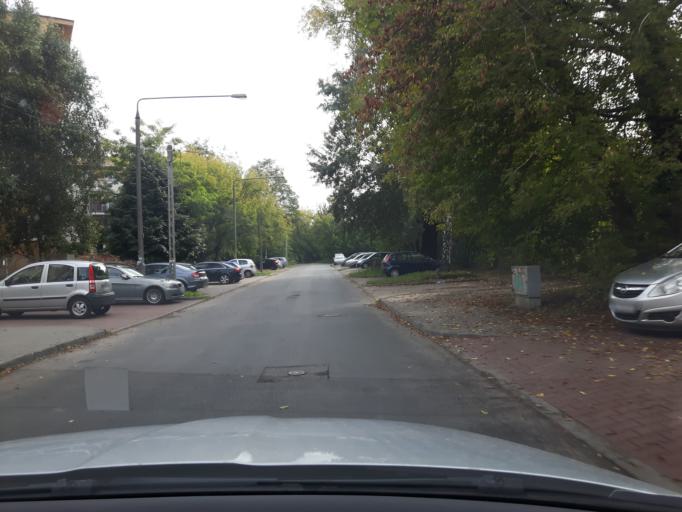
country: PL
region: Masovian Voivodeship
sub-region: Warszawa
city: Praga Polnoc
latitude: 52.2674
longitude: 21.0442
